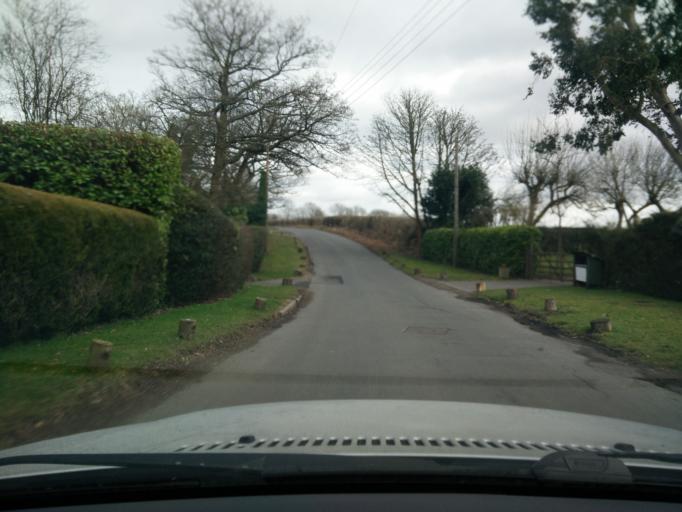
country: GB
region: England
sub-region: Buckinghamshire
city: Amersham
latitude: 51.6585
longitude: -0.6621
